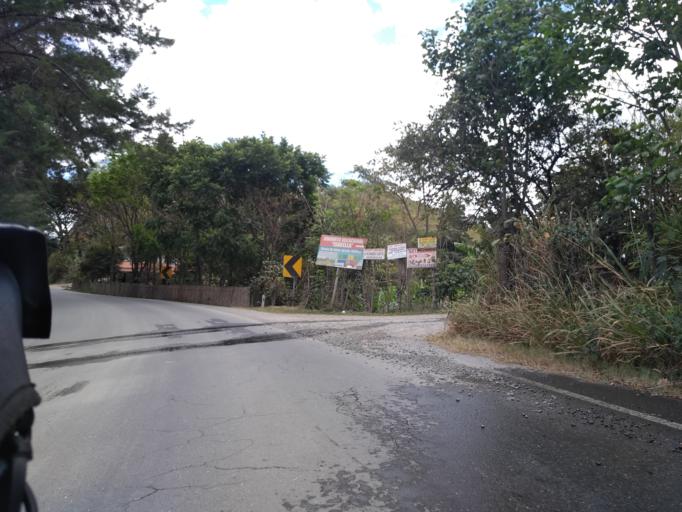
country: EC
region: Loja
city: Loja
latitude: -4.2114
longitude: -79.2332
